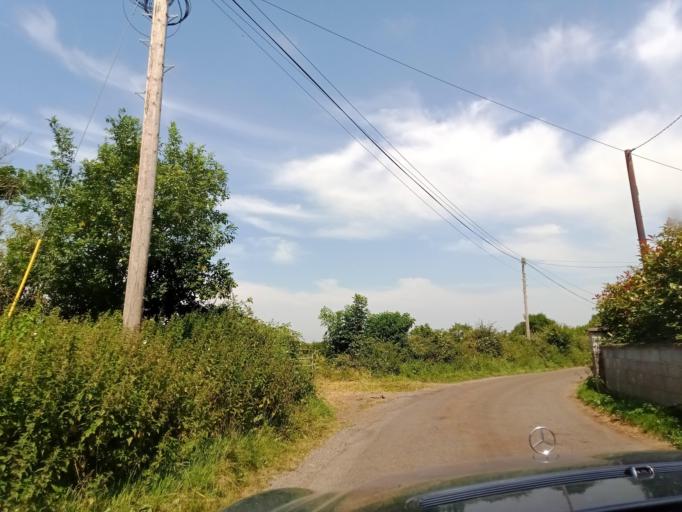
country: IE
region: Leinster
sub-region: Kilkenny
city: Mooncoin
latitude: 52.2695
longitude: -7.2358
